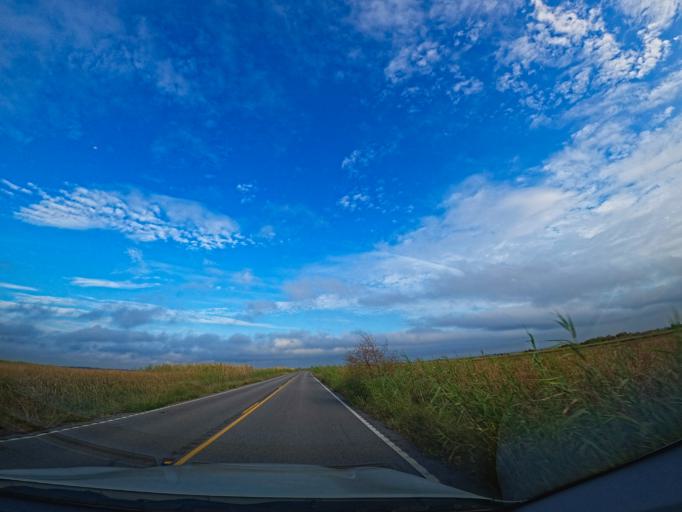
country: US
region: Louisiana
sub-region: Terrebonne Parish
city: Dulac
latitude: 29.3233
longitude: -90.6821
